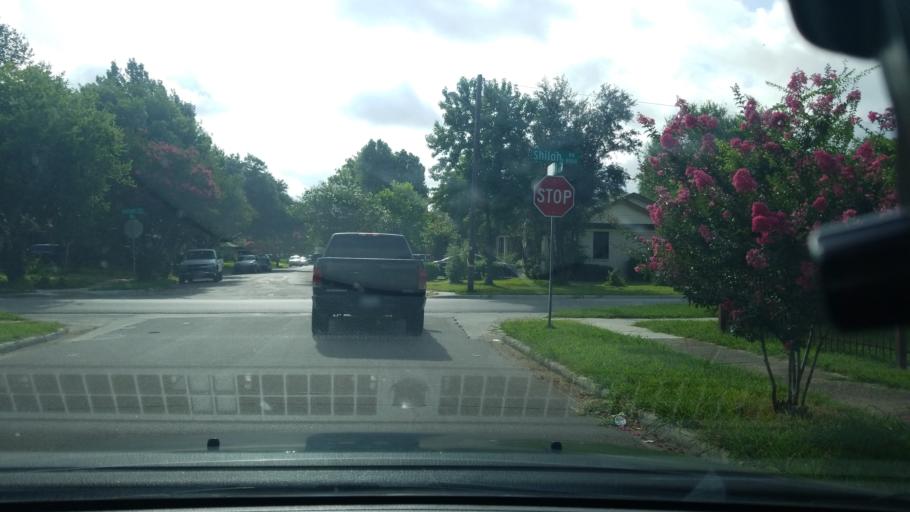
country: US
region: Texas
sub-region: Dallas County
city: Mesquite
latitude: 32.8197
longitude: -96.6687
